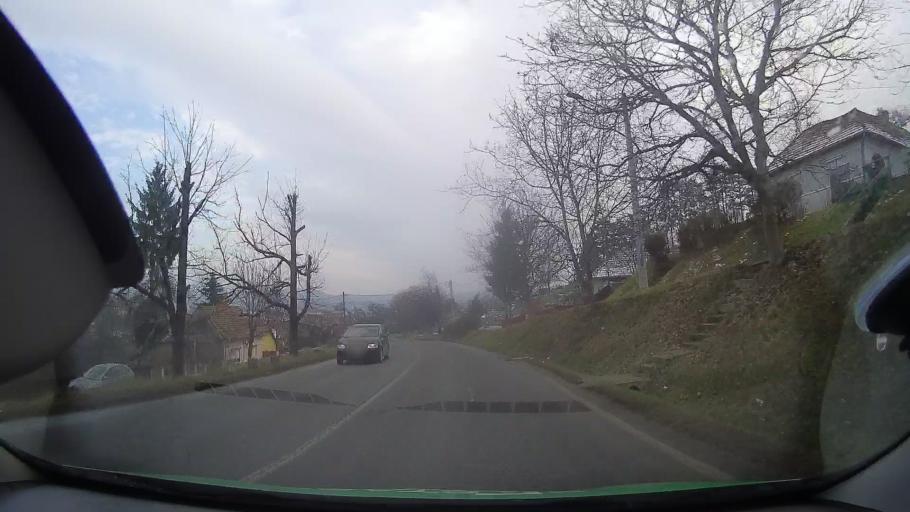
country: RO
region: Mures
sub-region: Municipiul Tarnaveni
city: Tarnaveni
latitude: 46.3366
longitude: 24.2863
